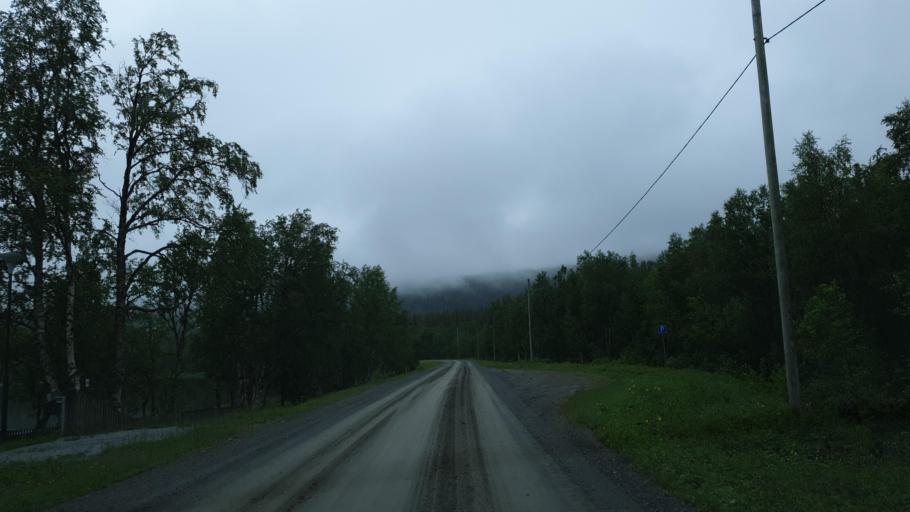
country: SE
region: Vaesterbotten
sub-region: Vilhelmina Kommun
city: Sjoberg
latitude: 65.3351
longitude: 15.8720
